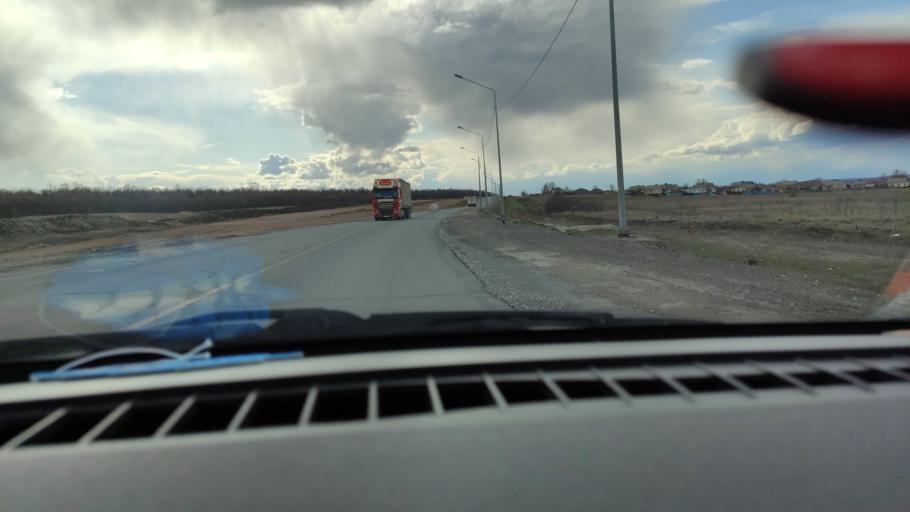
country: RU
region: Saratov
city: Sennoy
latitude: 52.1585
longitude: 47.0671
